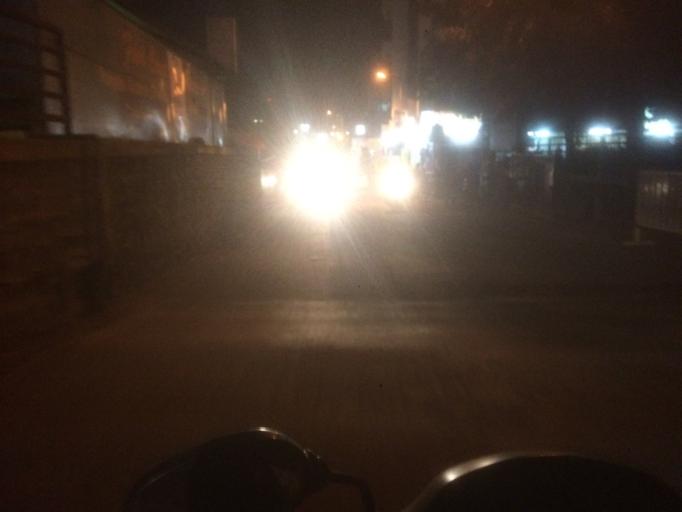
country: IN
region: Maharashtra
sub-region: Pune Division
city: Pune
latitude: 18.4638
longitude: 73.8366
